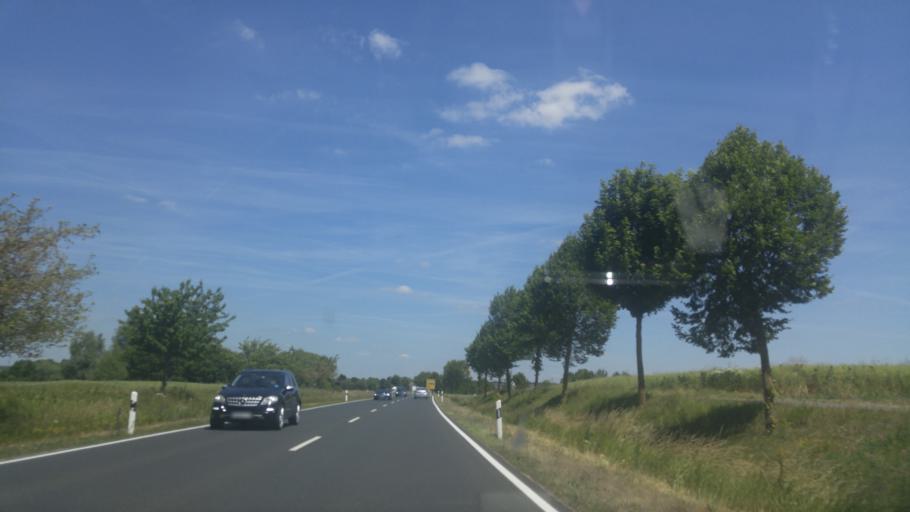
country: DE
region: Bavaria
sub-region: Regierungsbezirk Mittelfranken
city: Illesheim
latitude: 49.4735
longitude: 10.3680
